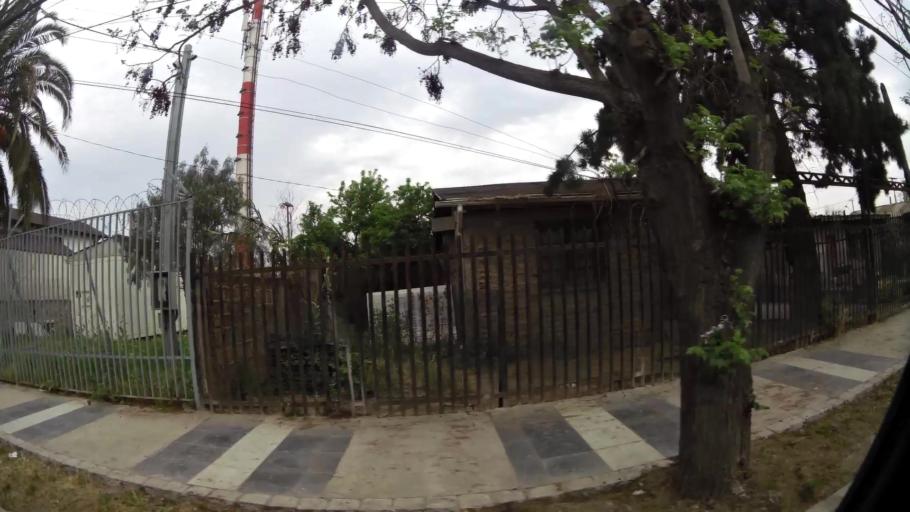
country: CL
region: Santiago Metropolitan
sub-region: Provincia de Santiago
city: Lo Prado
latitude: -33.5119
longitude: -70.7626
